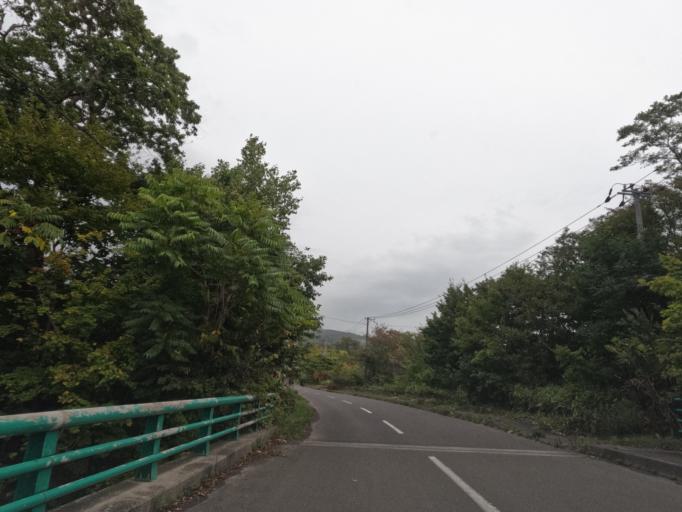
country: JP
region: Hokkaido
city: Date
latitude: 42.4553
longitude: 140.9035
